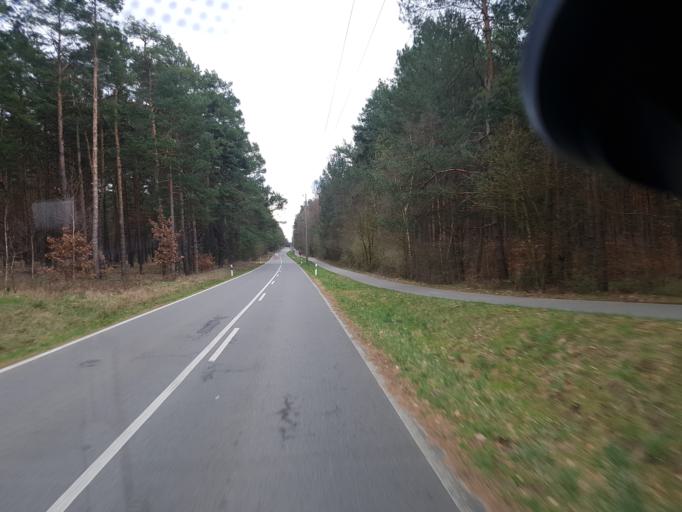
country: DE
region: Brandenburg
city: Mixdorf
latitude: 52.1913
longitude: 14.4198
